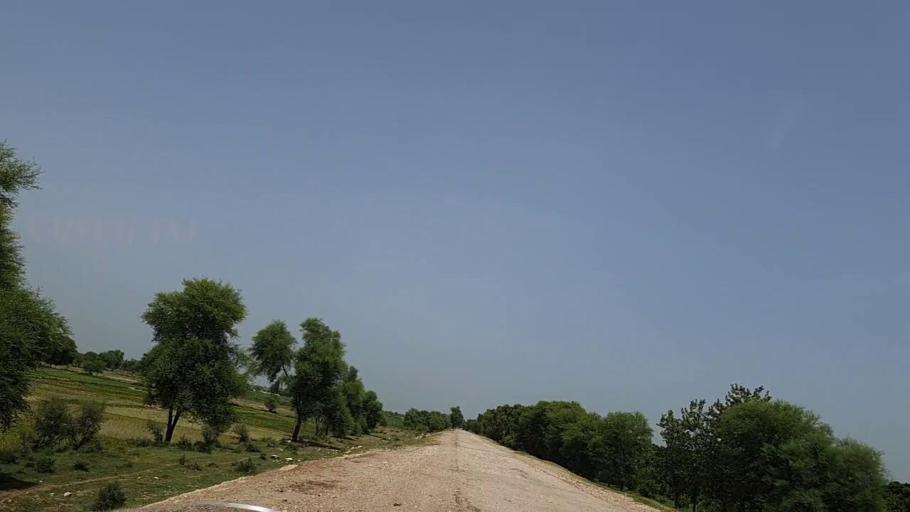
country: PK
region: Sindh
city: Tharu Shah
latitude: 27.0033
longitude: 68.0942
